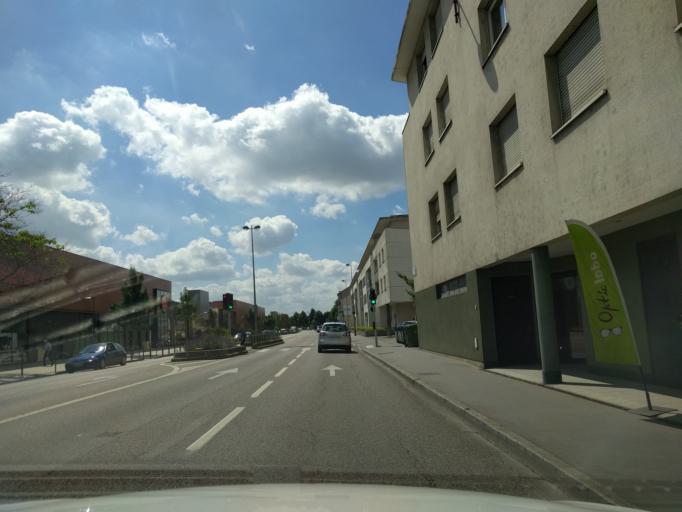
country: FR
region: Lorraine
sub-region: Departement de Meurthe-et-Moselle
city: Nancy
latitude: 48.6818
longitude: 6.1976
